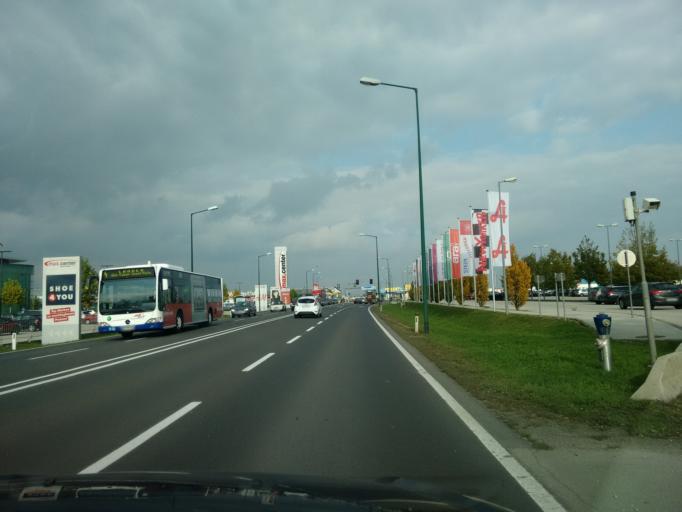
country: AT
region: Upper Austria
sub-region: Wels-Land
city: Gunskirchen
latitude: 48.1450
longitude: 13.9734
